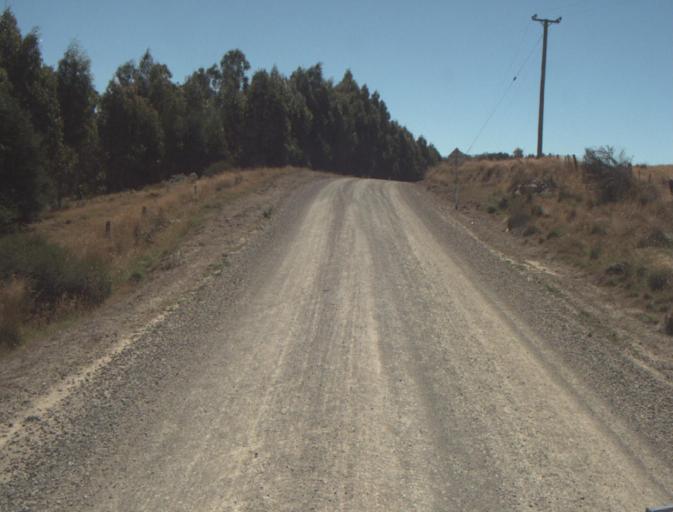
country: AU
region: Tasmania
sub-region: Dorset
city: Scottsdale
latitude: -41.3564
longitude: 147.4570
